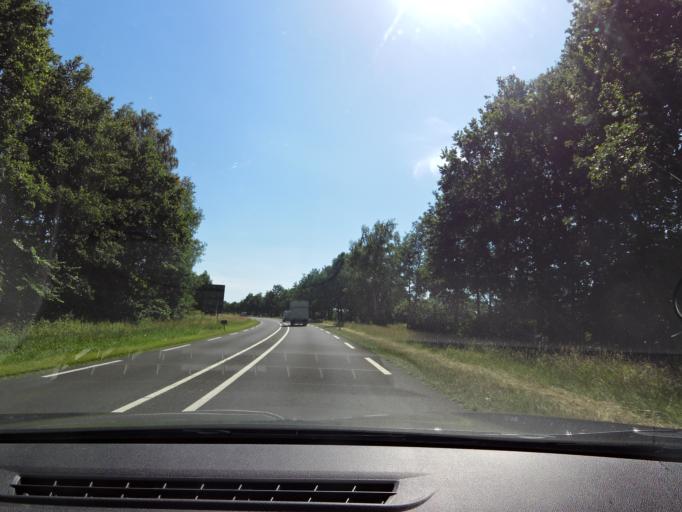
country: NL
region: Gelderland
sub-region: Oost Gelre
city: Lichtenvoorde
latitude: 52.0301
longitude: 6.6149
